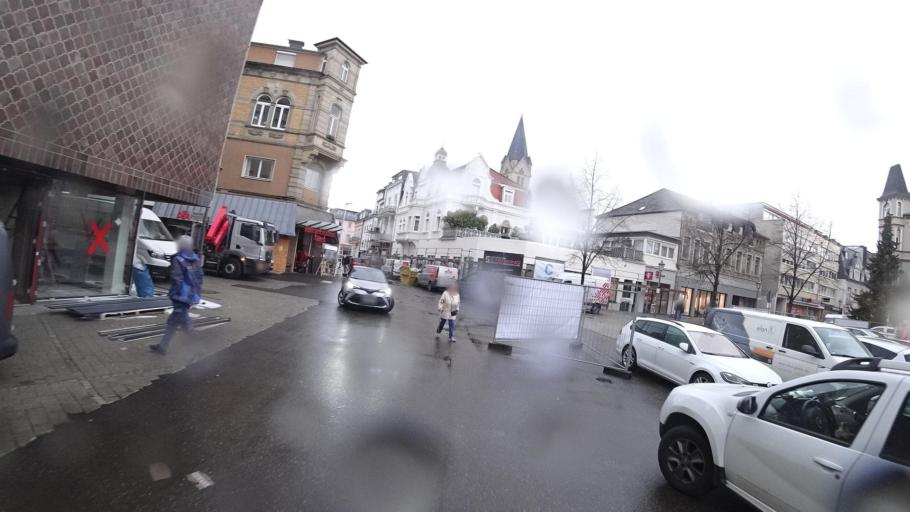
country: DE
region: Rheinland-Pfalz
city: Bad Neuenahr-Ahrweiler
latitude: 50.5447
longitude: 7.1377
